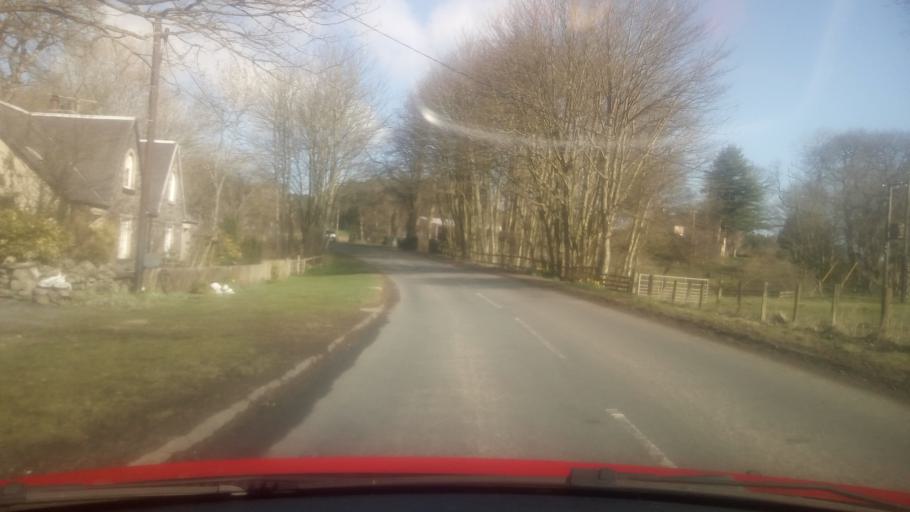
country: GB
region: Scotland
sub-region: The Scottish Borders
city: Selkirk
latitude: 55.5694
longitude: -2.8369
